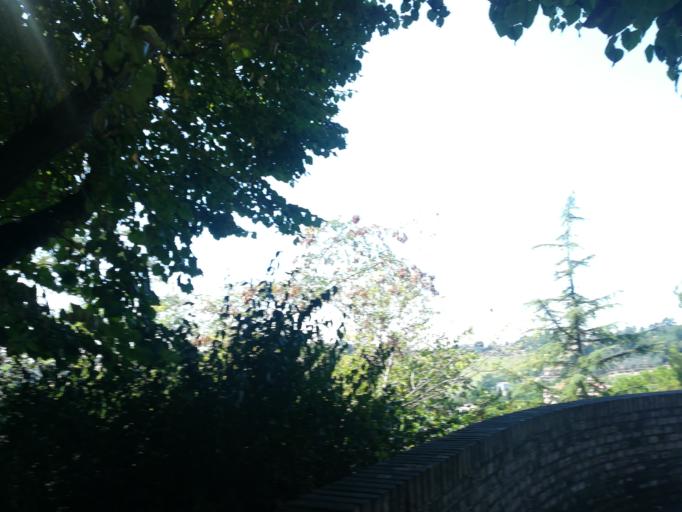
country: IT
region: The Marches
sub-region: Provincia di Ancona
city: Corinaldo
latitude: 43.6503
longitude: 13.0461
